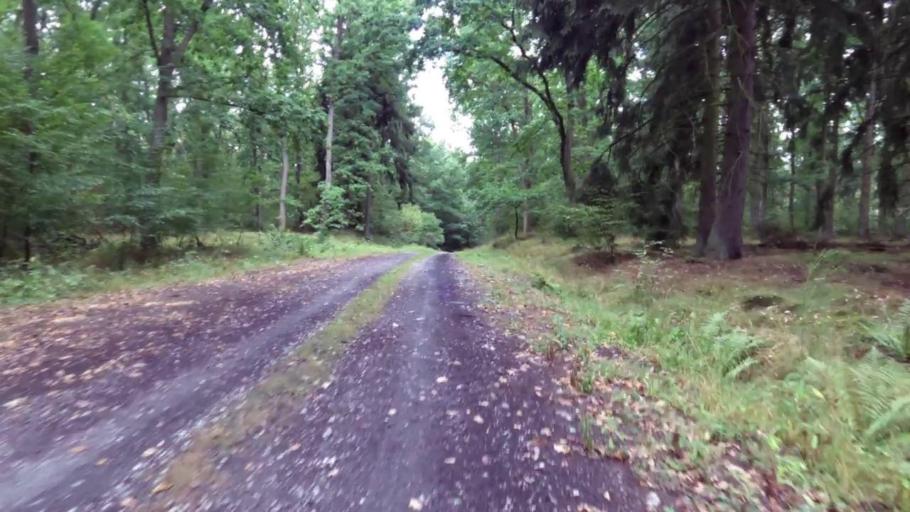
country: PL
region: West Pomeranian Voivodeship
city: Trzcinsko Zdroj
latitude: 52.8787
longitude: 14.6828
